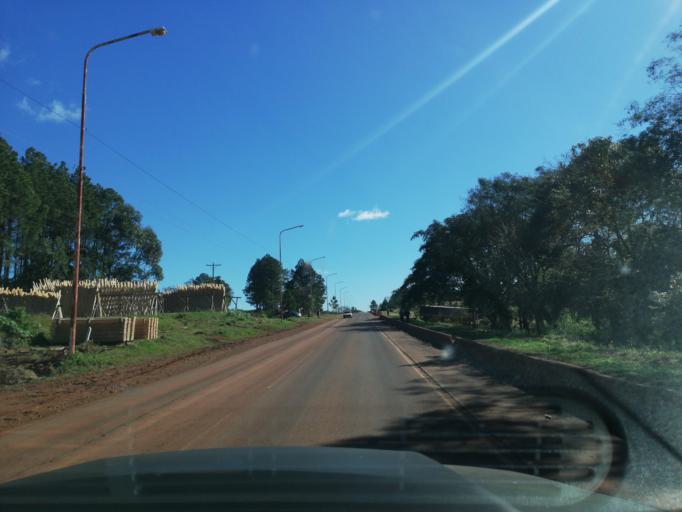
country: AR
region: Misiones
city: Aristobulo del Valle
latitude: -27.0901
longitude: -54.9100
